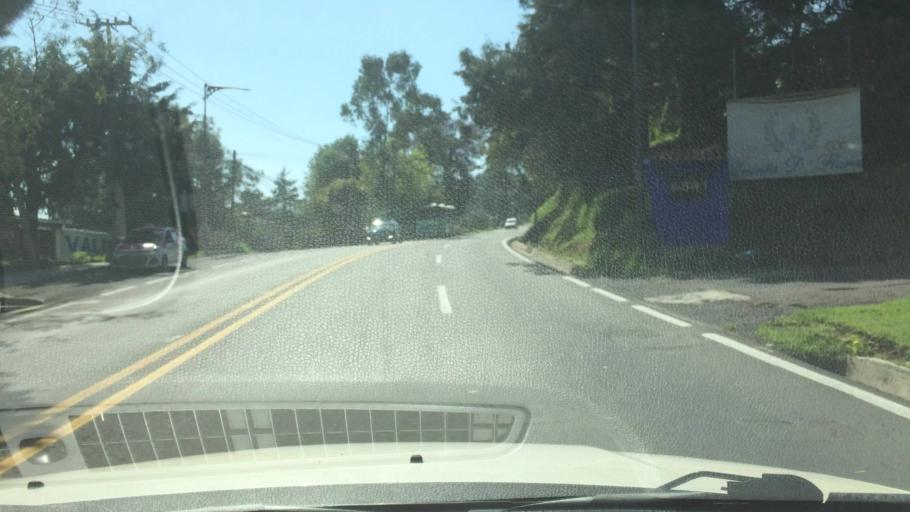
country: MX
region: Mexico City
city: Tlalpan
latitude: 19.2414
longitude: -99.1643
